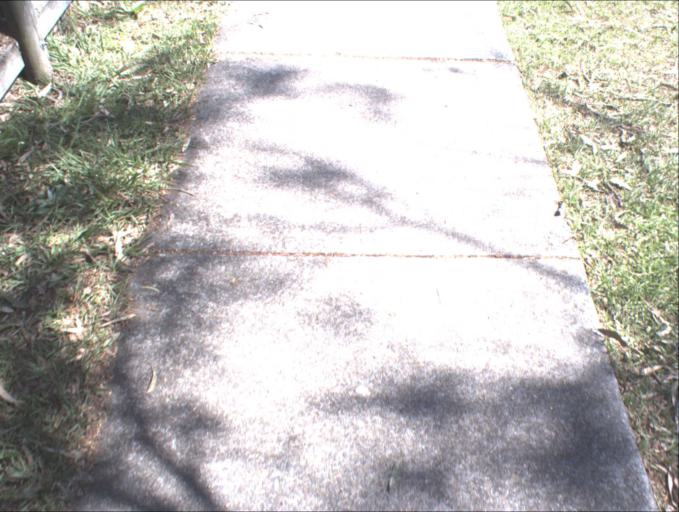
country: AU
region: Queensland
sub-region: Logan
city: Beenleigh
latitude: -27.7008
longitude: 153.1688
